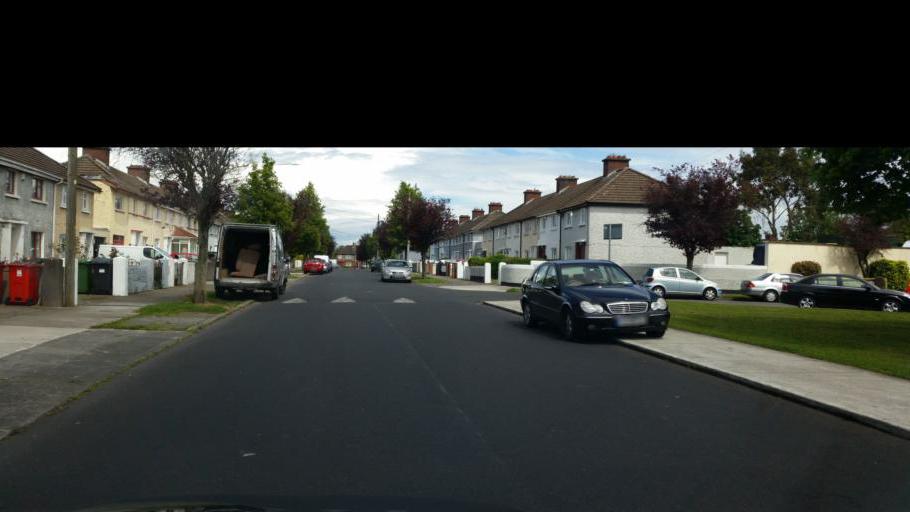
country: IE
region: Leinster
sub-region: Dublin City
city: Finglas
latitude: 53.3928
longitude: -6.2921
